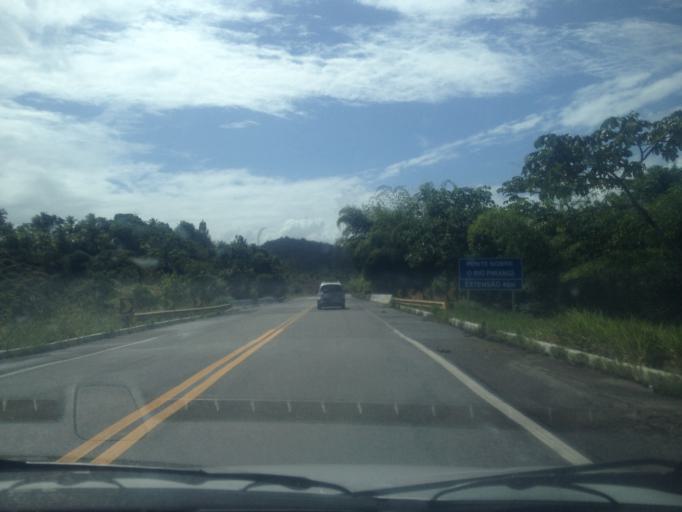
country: BR
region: Bahia
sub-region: Conde
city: Conde
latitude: -11.6944
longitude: -37.5707
